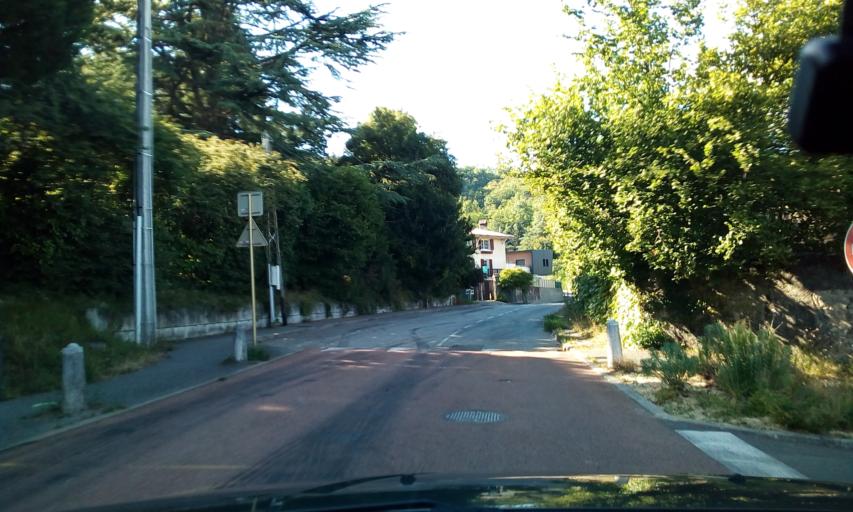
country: FR
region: Rhone-Alpes
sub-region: Departement de l'Isere
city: Seyssins
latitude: 45.1574
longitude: 5.6786
